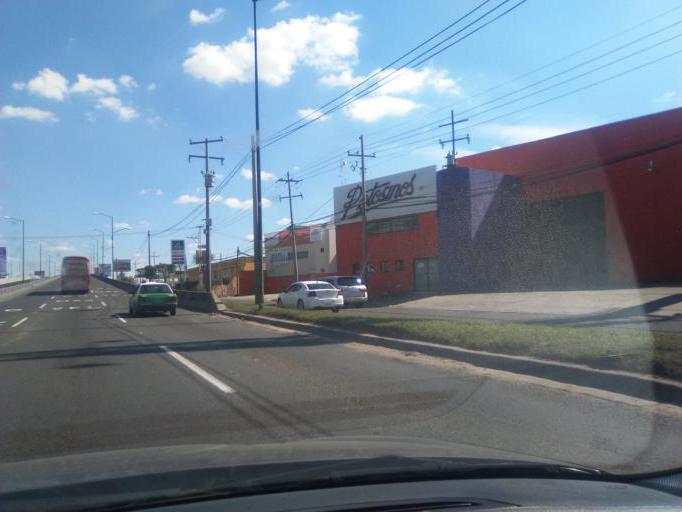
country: MX
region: Guanajuato
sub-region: Leon
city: Fraccionamiento Paraiso Real
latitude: 21.0922
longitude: -101.6231
